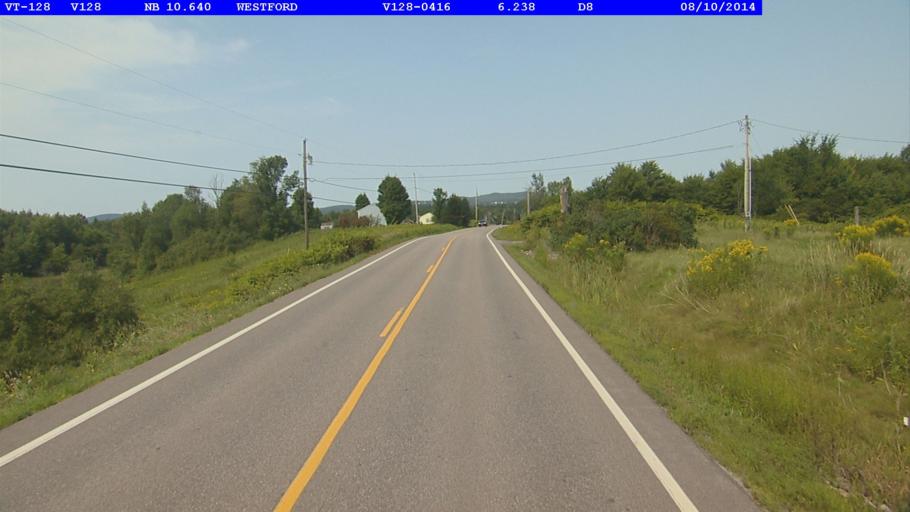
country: US
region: Vermont
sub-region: Chittenden County
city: Milton
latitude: 44.6429
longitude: -73.0155
